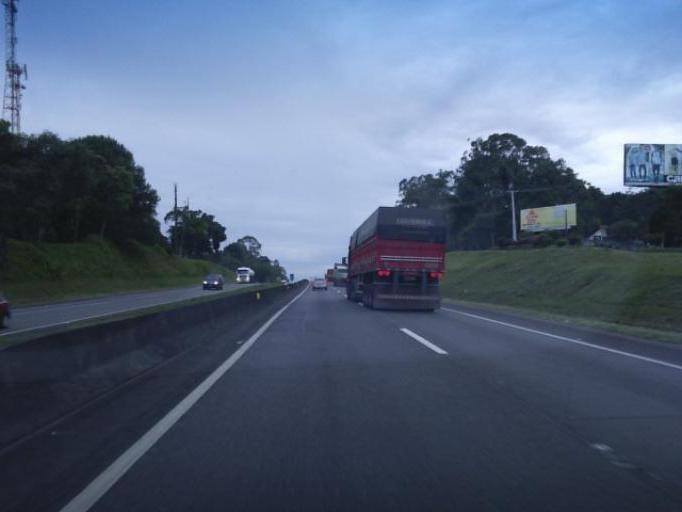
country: BR
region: Parana
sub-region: Sao Jose Dos Pinhais
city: Sao Jose dos Pinhais
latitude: -25.7193
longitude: -49.1374
